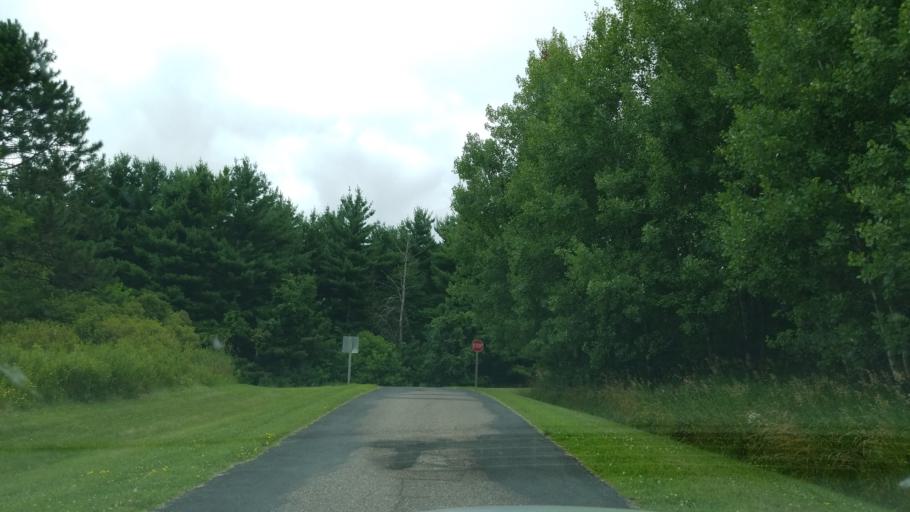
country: US
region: Wisconsin
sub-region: Saint Croix County
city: Glenwood City
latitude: 45.0107
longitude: -92.1650
